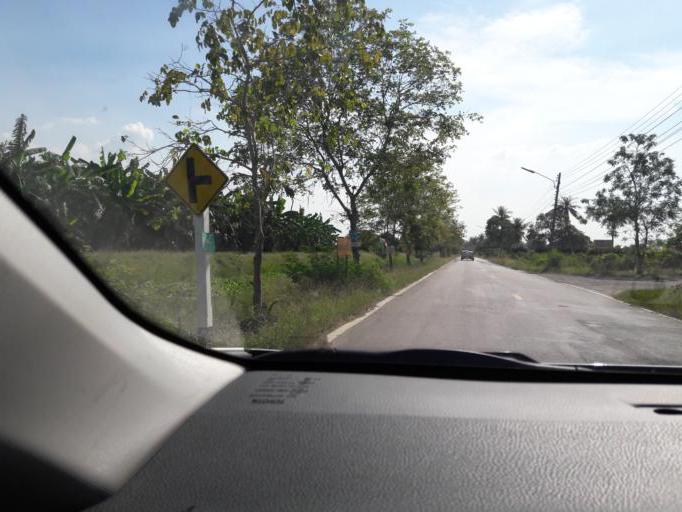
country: TH
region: Ang Thong
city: Ang Thong
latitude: 14.5873
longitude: 100.3989
